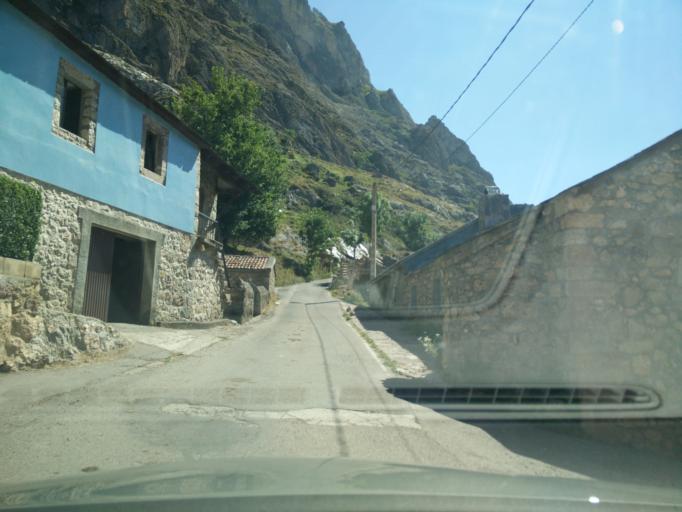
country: ES
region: Asturias
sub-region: Province of Asturias
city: Pola de Somiedo
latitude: 43.0720
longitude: -6.1977
